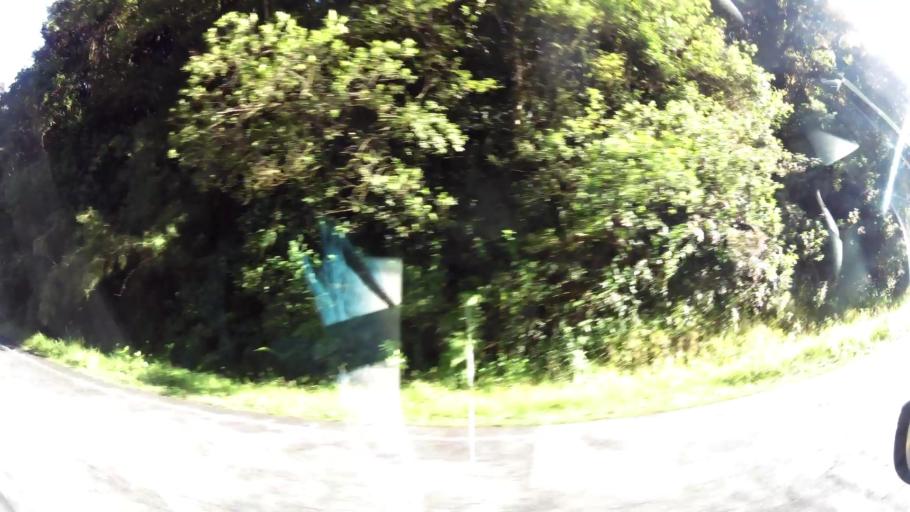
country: CR
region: San Jose
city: San Marcos
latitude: 9.7124
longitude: -83.9501
